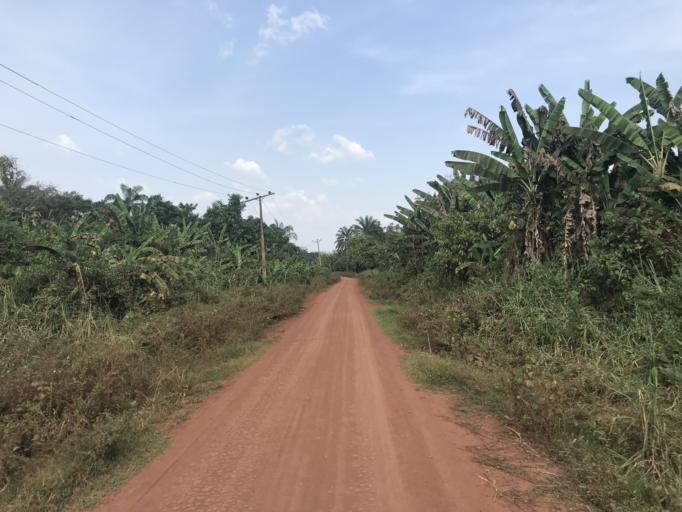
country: NG
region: Osun
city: Ilesa
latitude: 7.6571
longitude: 4.6713
